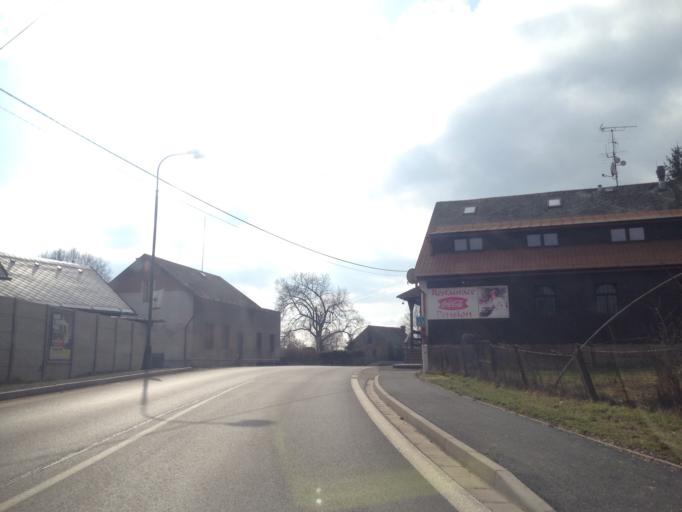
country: CZ
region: Kralovehradecky
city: Nova Paka
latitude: 50.5026
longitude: 15.5321
